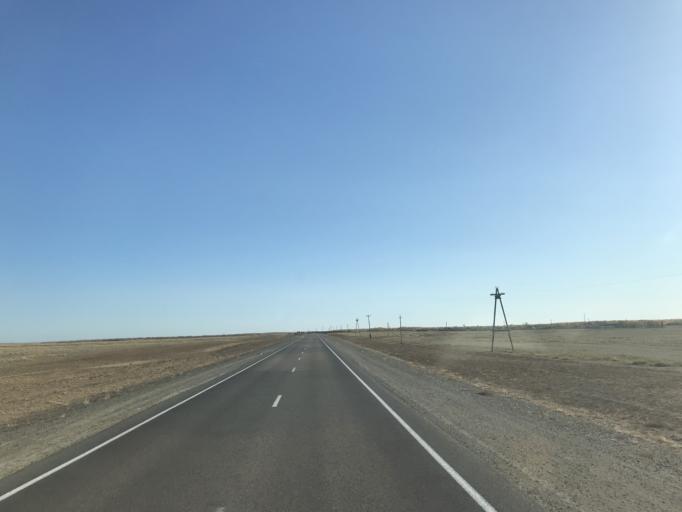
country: KZ
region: Pavlodar
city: Koktobe
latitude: 51.5481
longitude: 77.6410
